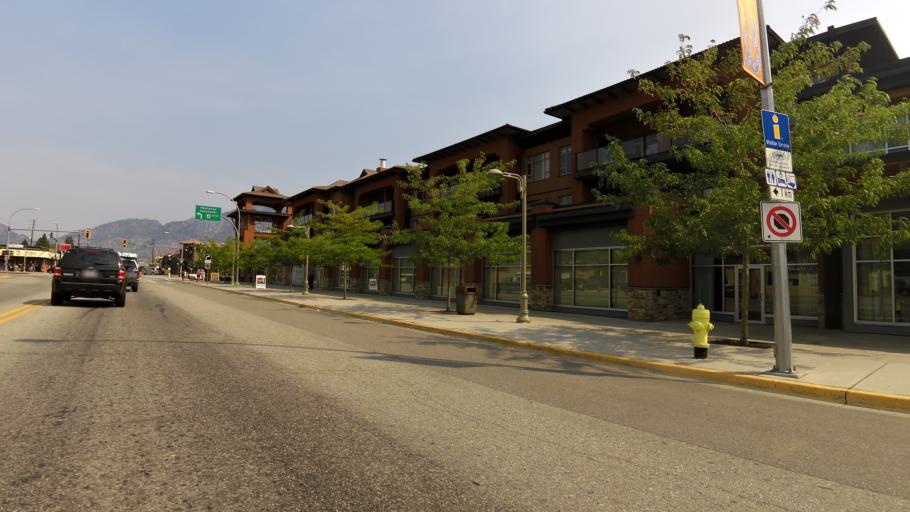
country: CA
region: British Columbia
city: Osoyoos
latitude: 49.0321
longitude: -119.4634
